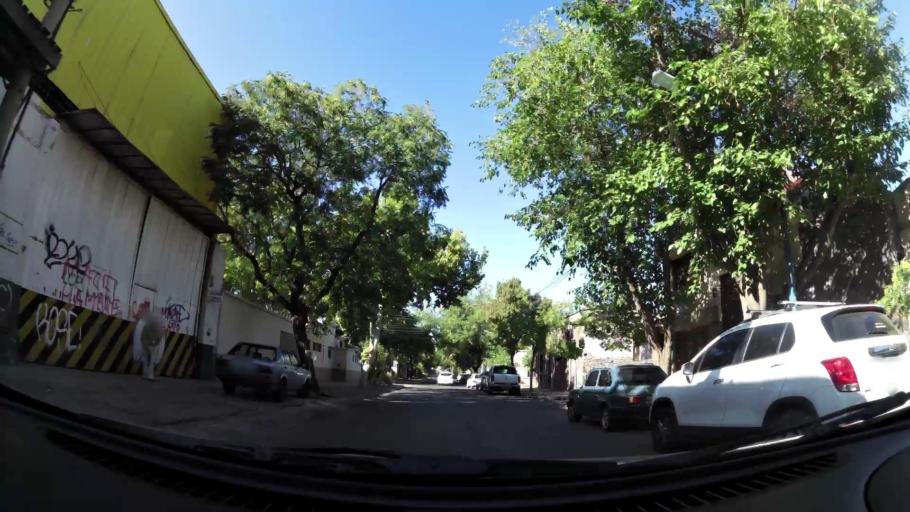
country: AR
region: Mendoza
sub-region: Departamento de Godoy Cruz
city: Godoy Cruz
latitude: -32.9138
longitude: -68.8468
